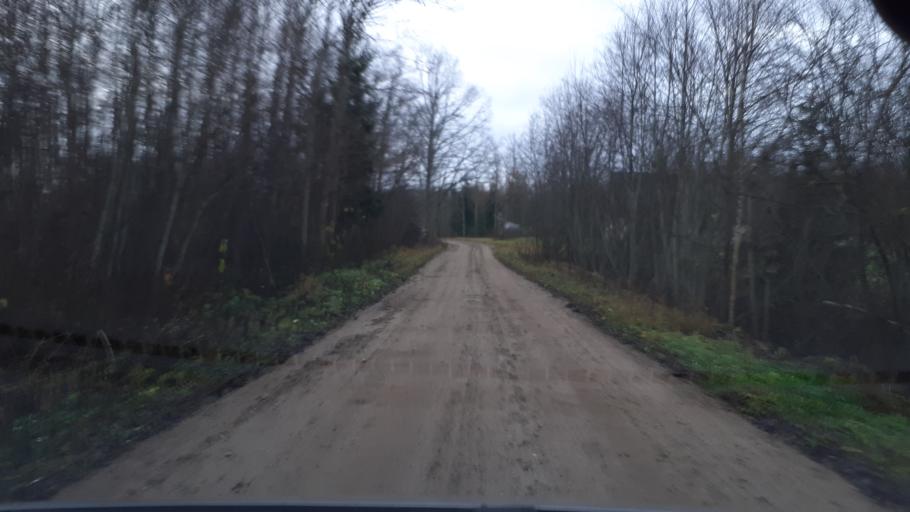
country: LV
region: Kuldigas Rajons
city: Kuldiga
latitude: 57.0029
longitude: 21.9210
